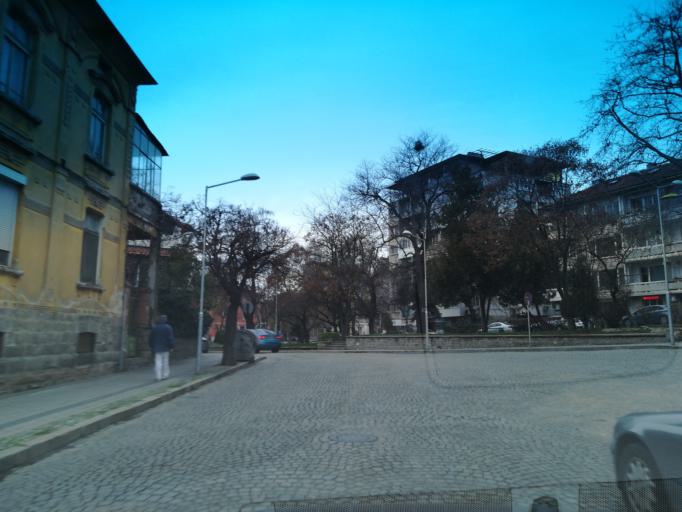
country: BG
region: Plovdiv
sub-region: Obshtina Plovdiv
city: Plovdiv
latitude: 42.1471
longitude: 24.7419
